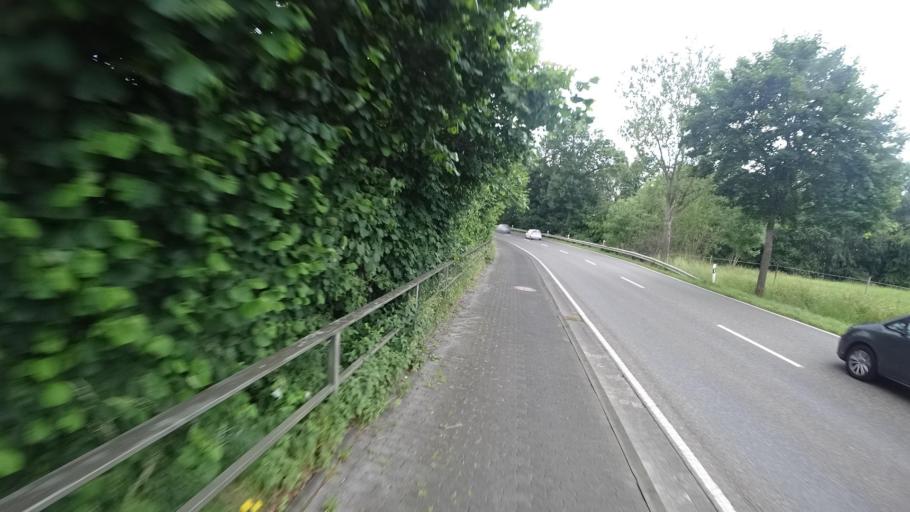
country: DE
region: Rheinland-Pfalz
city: Mammelzen
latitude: 50.7052
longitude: 7.6696
